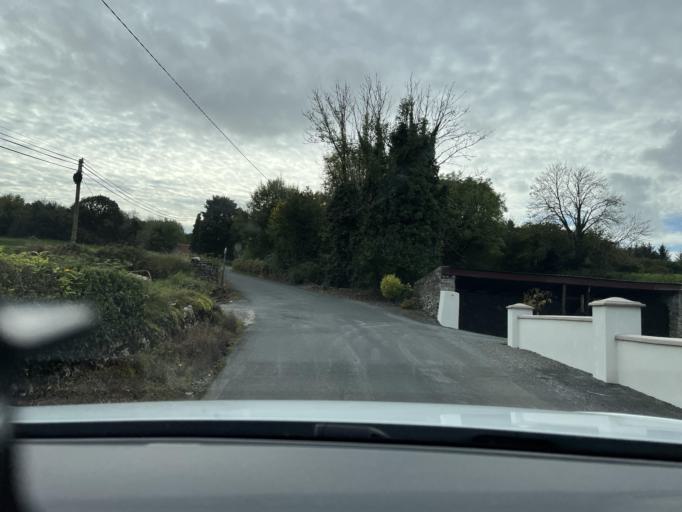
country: IE
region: Connaught
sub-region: Roscommon
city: Boyle
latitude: 54.0219
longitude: -8.3454
